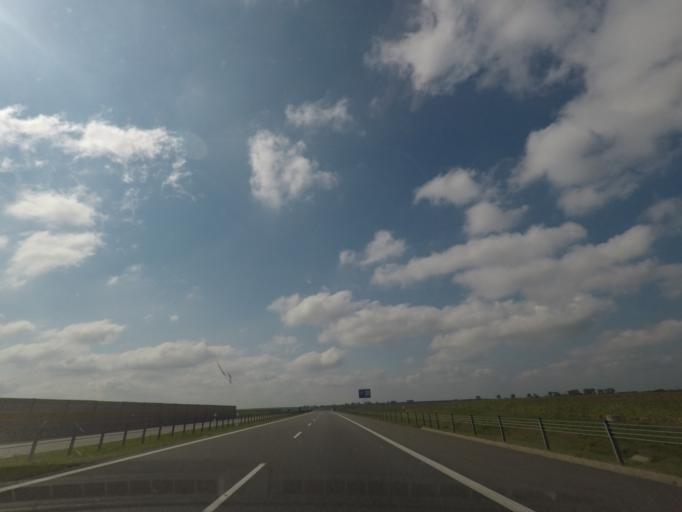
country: PL
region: Kujawsko-Pomorskie
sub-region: Powiat wabrzeski
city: Pluznica
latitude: 53.1911
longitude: 18.7383
